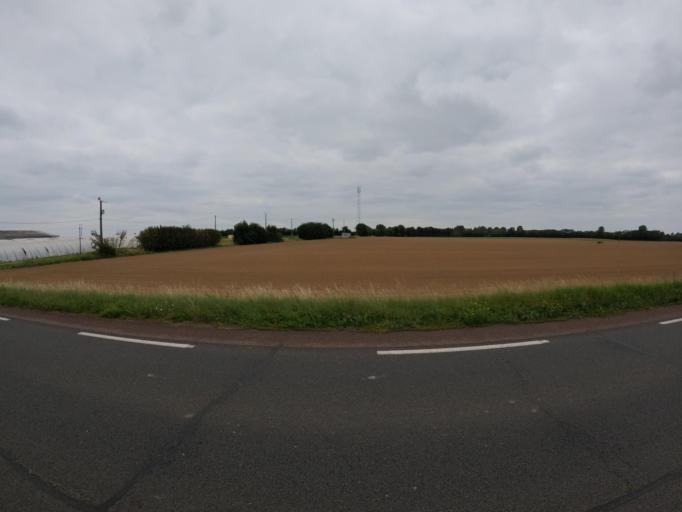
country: FR
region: Pays de la Loire
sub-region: Departement de la Vendee
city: Maillezais
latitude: 46.4098
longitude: -0.6858
